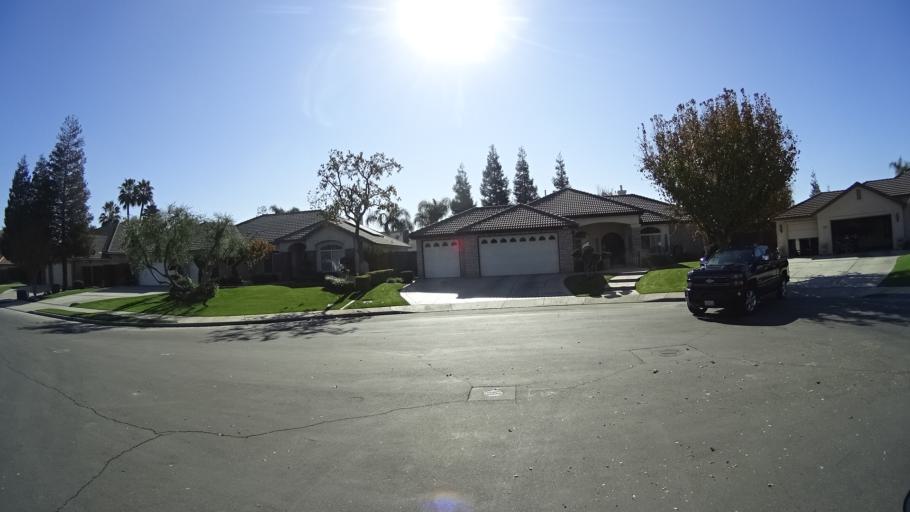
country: US
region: California
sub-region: Kern County
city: Rosedale
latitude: 35.3653
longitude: -119.1384
